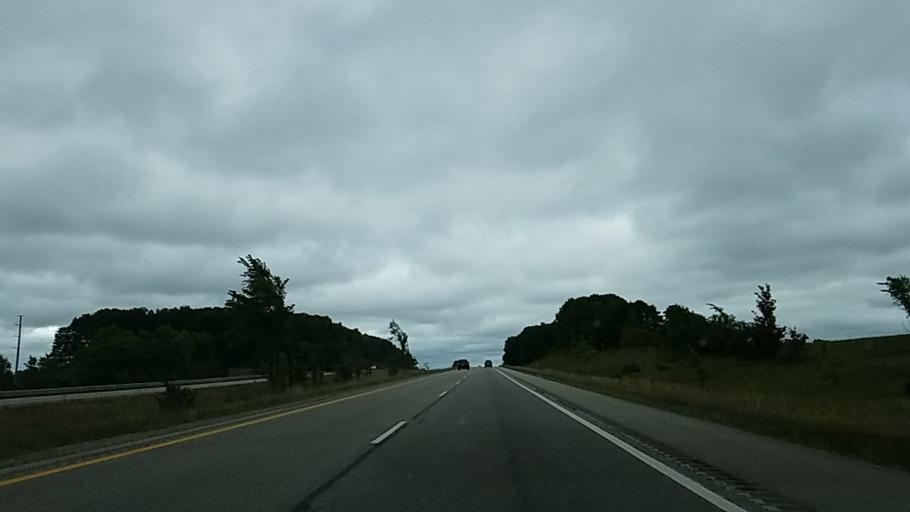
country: US
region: Michigan
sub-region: Otsego County
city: Gaylord
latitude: 45.0663
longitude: -84.6892
